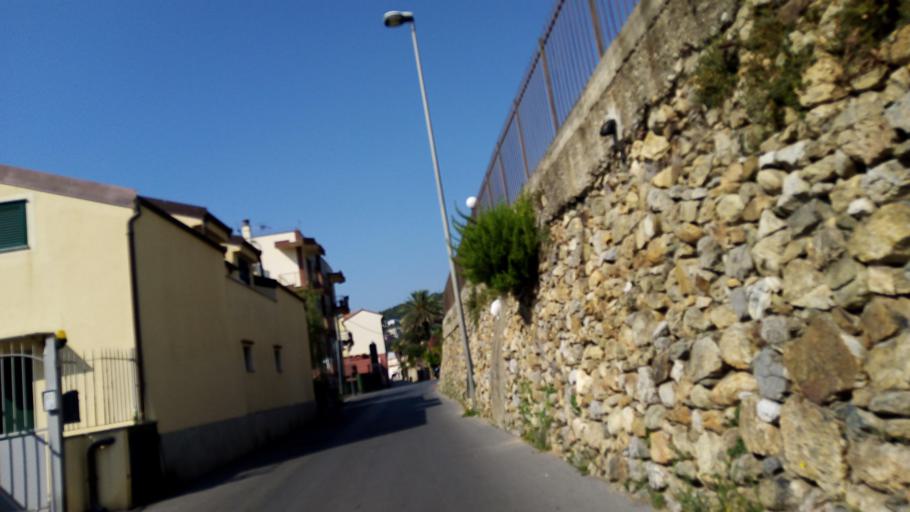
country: IT
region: Liguria
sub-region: Provincia di Savona
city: Pietra Ligure
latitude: 44.1565
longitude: 8.2941
